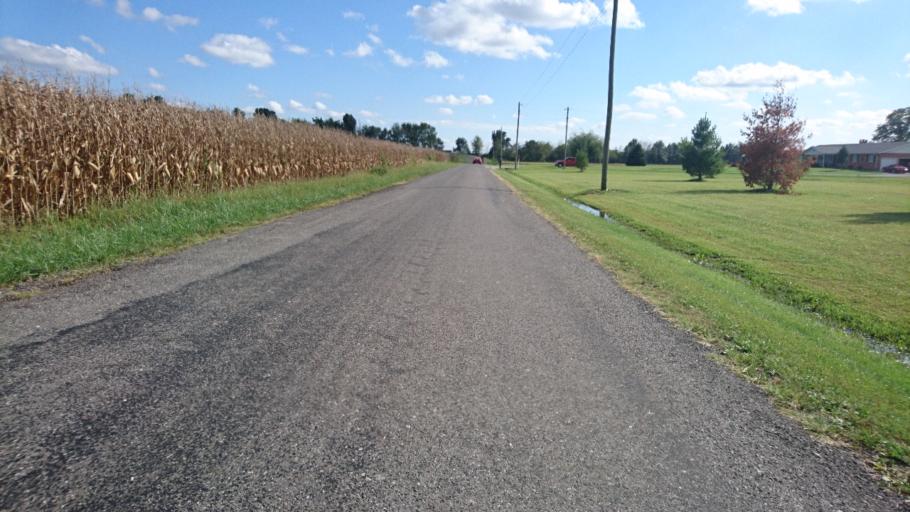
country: US
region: Illinois
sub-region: Macoupin County
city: Staunton
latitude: 38.9928
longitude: -89.7317
